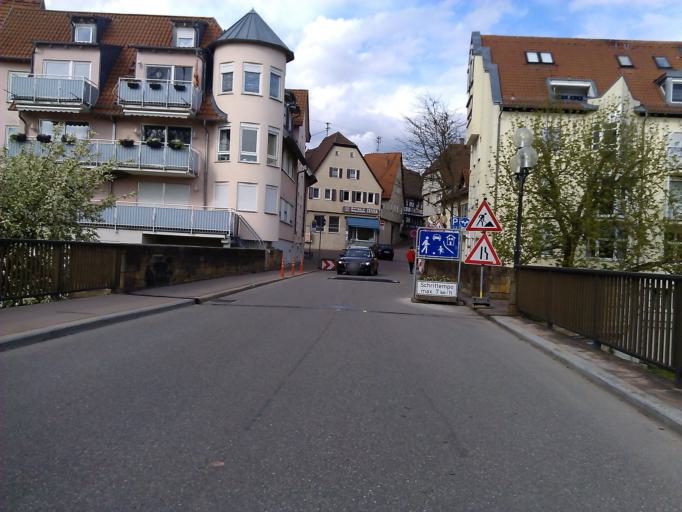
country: DE
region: Baden-Wuerttemberg
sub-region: Regierungsbezirk Stuttgart
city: Lauffen am Neckar
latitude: 49.0756
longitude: 9.1580
